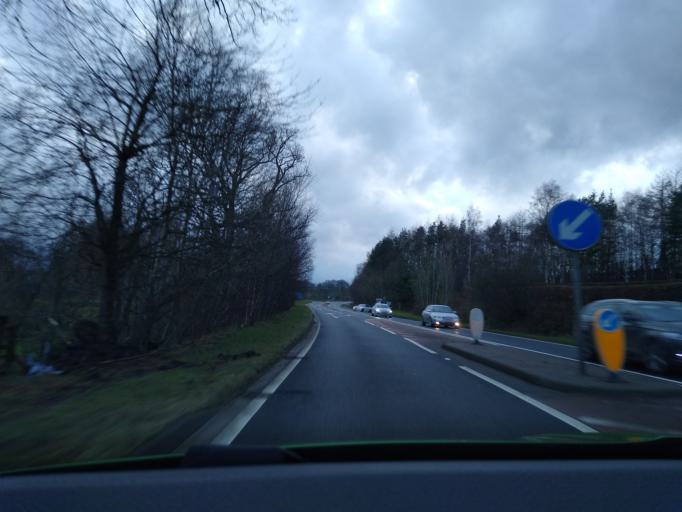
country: GB
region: England
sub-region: Cumbria
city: Keswick
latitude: 54.6156
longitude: -3.0589
